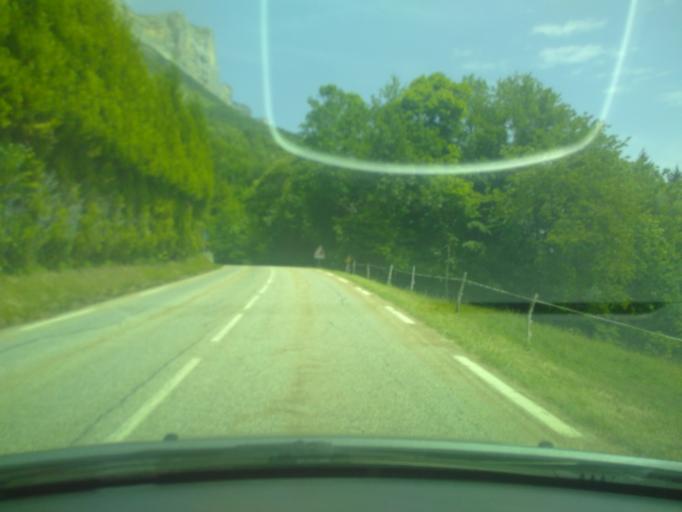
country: FR
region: Rhone-Alpes
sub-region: Departement de l'Isere
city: Crolles
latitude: 45.2947
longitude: 5.8644
